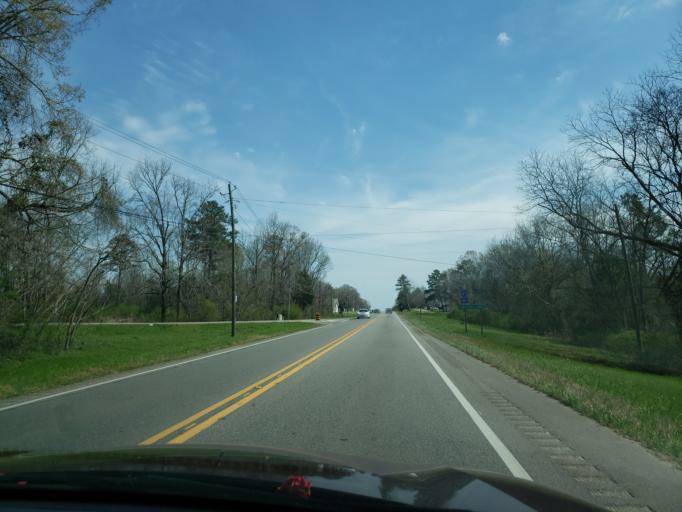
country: US
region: Alabama
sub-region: Autauga County
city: Prattville
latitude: 32.4304
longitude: -86.5403
